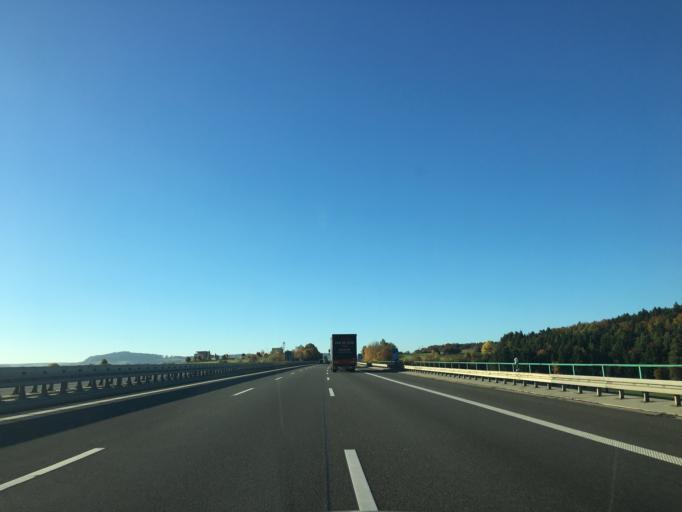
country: DE
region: Baden-Wuerttemberg
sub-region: Freiburg Region
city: Engen
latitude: 47.8573
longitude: 8.7940
